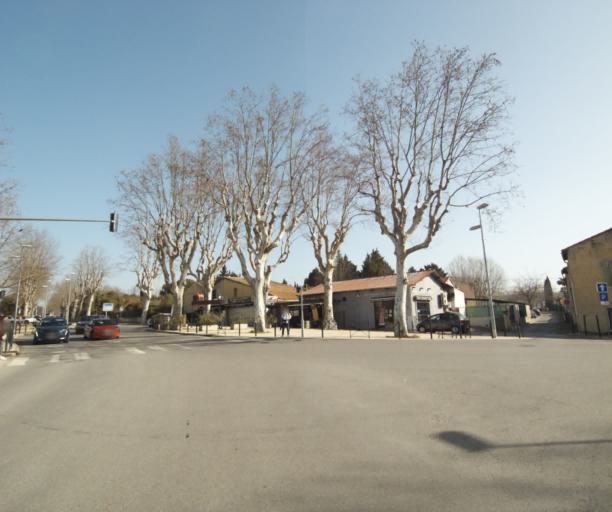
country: FR
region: Provence-Alpes-Cote d'Azur
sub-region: Departement des Bouches-du-Rhone
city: Aix-en-Provence
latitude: 43.5553
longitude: 5.4594
